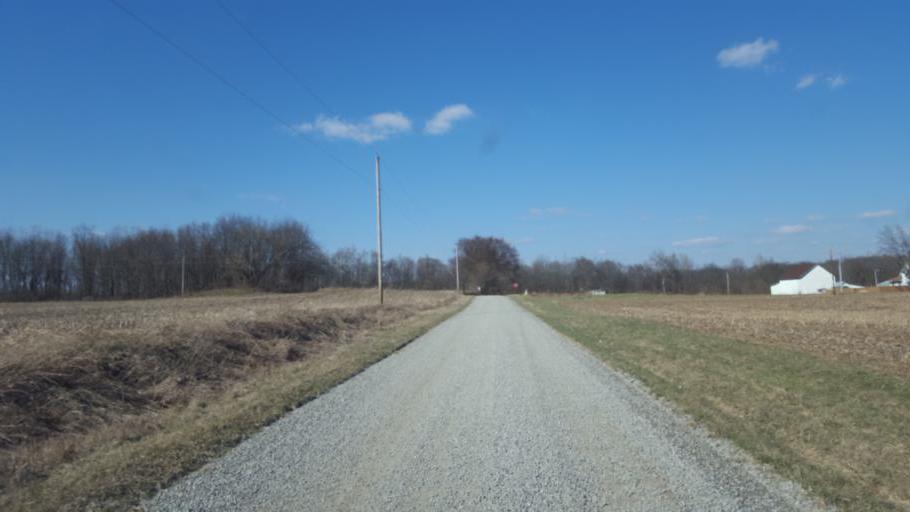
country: US
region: Ohio
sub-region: Morrow County
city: Mount Gilead
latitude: 40.4730
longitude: -82.7444
